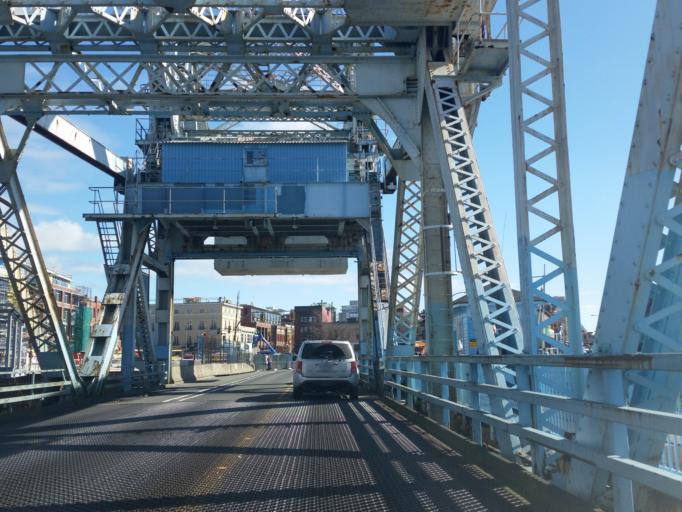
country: CA
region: British Columbia
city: Victoria
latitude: 48.4280
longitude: -123.3721
